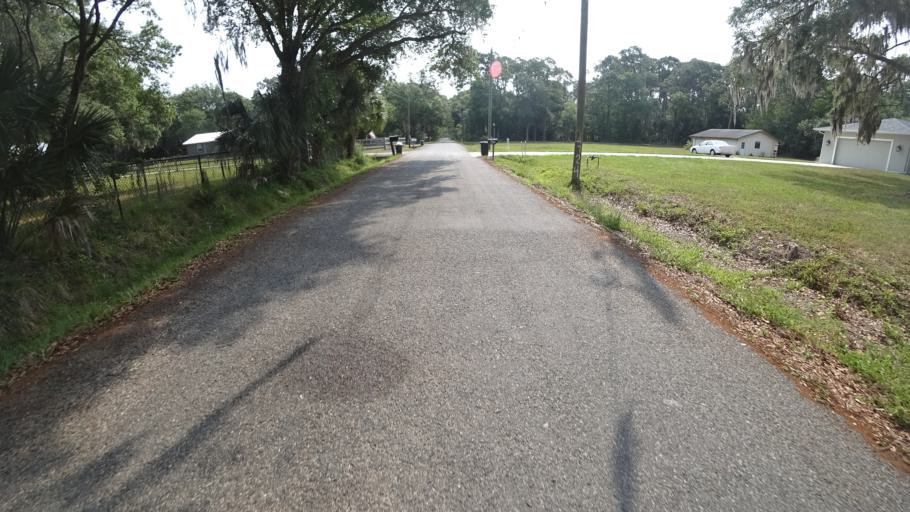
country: US
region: Florida
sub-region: Manatee County
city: Samoset
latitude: 27.4730
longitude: -82.5025
